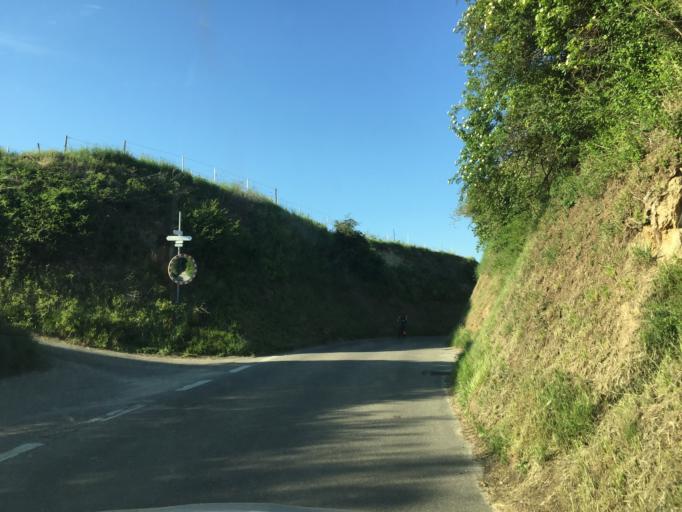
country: DE
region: Baden-Wuerttemberg
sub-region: Freiburg Region
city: Vogtsburg
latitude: 48.0776
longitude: 7.6395
